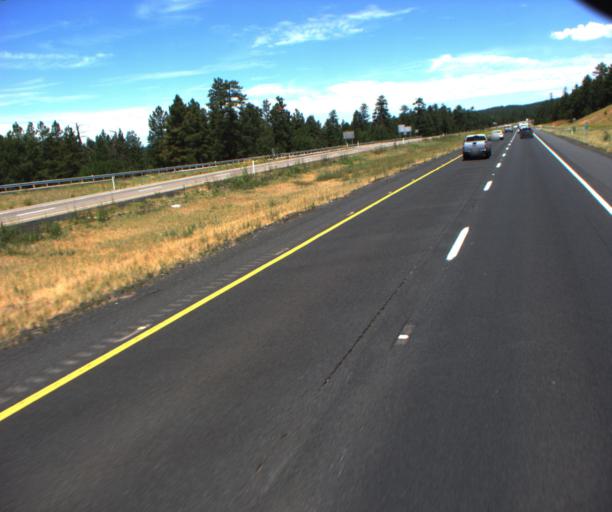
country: US
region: Arizona
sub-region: Coconino County
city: Sedona
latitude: 34.8762
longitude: -111.6356
